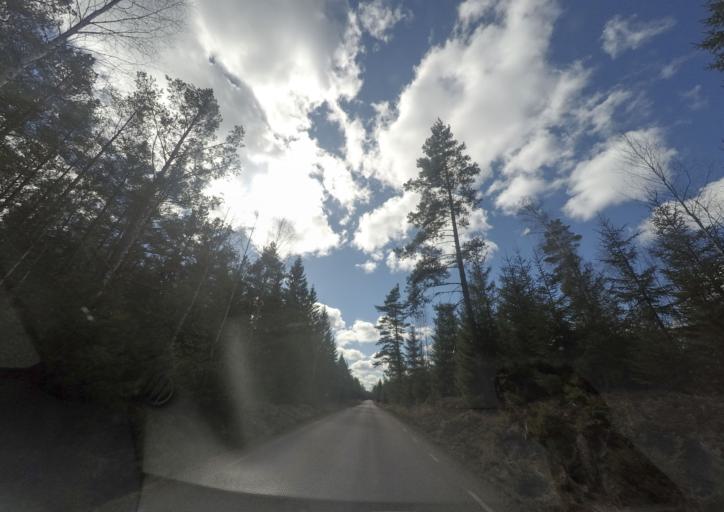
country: SE
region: OEstergoetland
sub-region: Norrkopings Kommun
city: Krokek
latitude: 58.7716
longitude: 16.4475
